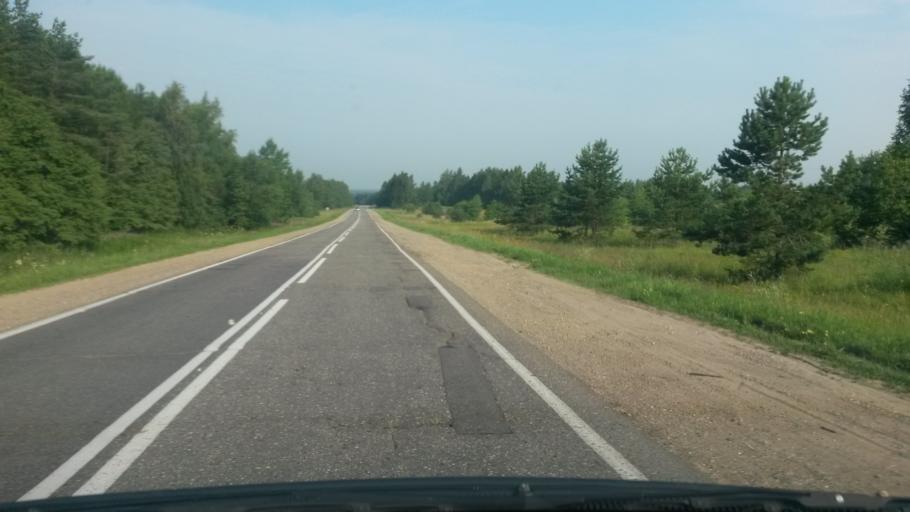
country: RU
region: Jaroslavl
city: Krasnyye Tkachi
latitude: 57.3765
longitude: 39.7211
